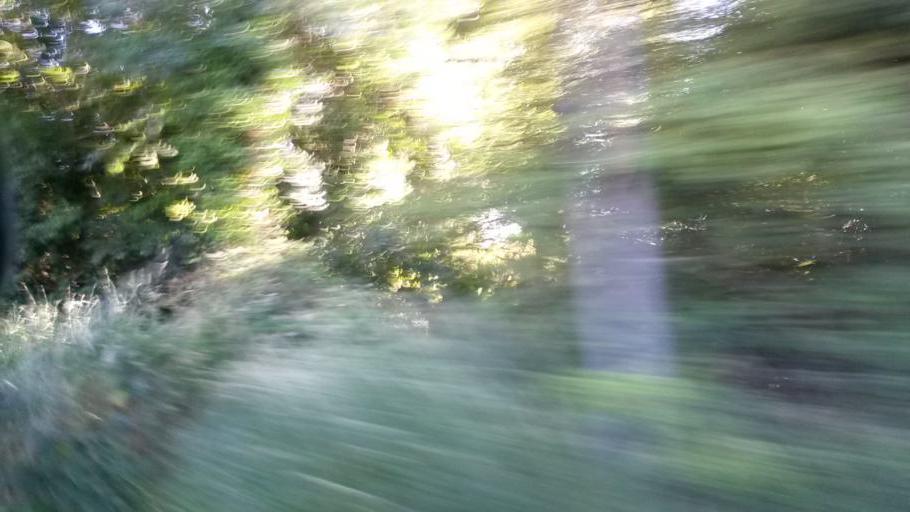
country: IE
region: Leinster
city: Ballymun
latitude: 53.4496
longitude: -6.2942
